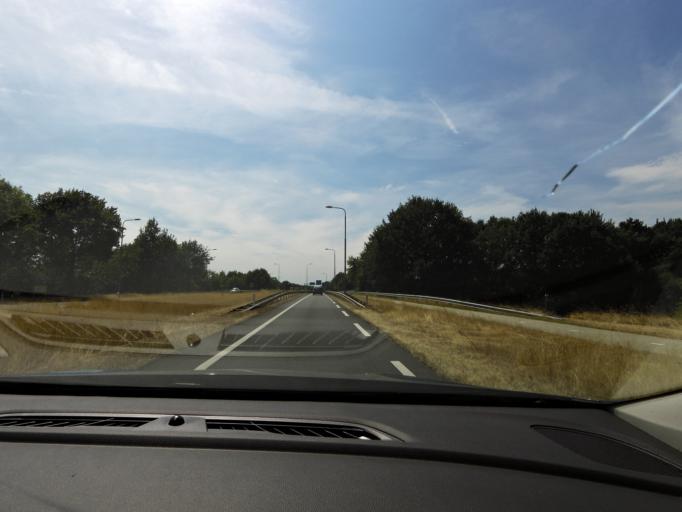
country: NL
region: Limburg
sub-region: Gemeente Leudal
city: Kelpen-Oler
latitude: 51.1809
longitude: 5.8504
